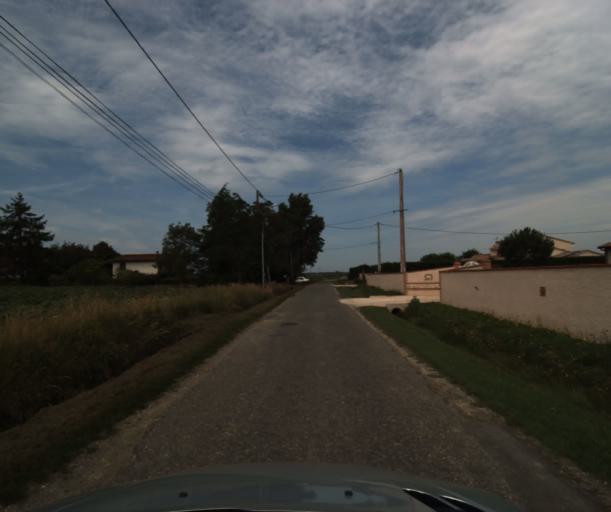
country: FR
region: Midi-Pyrenees
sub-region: Departement de la Haute-Garonne
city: Lacasse
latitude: 43.4180
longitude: 1.2682
